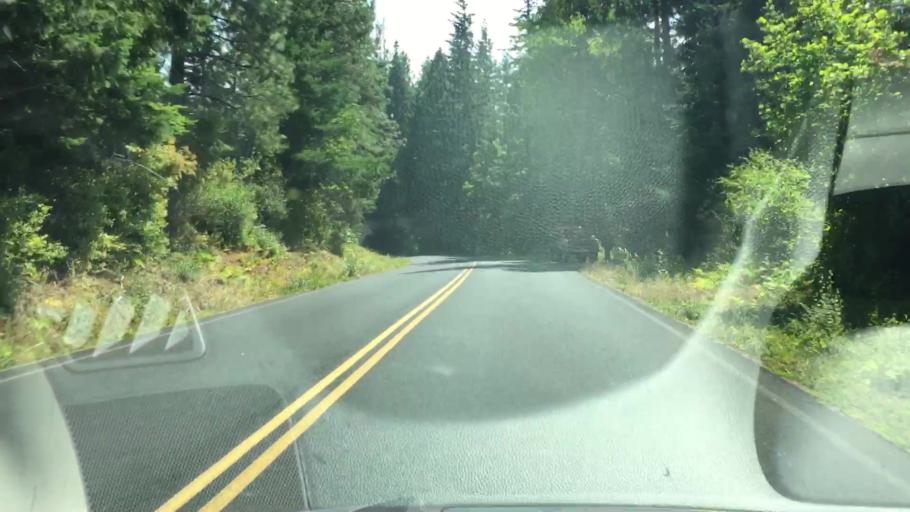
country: US
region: Washington
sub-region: Klickitat County
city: White Salmon
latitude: 46.0369
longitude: -121.5462
